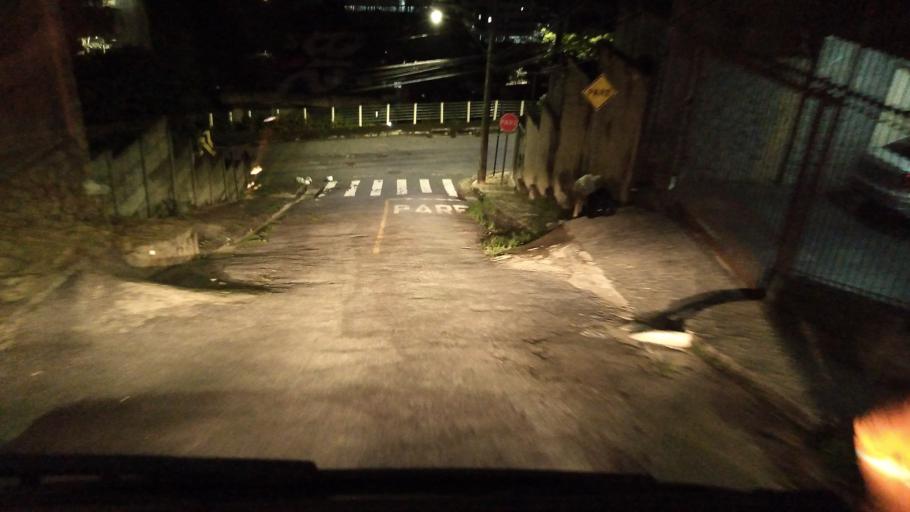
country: BR
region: Minas Gerais
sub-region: Belo Horizonte
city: Belo Horizonte
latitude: -19.8995
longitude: -43.9753
